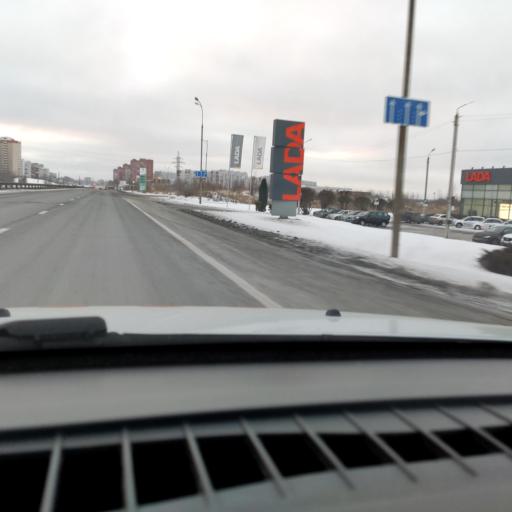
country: RU
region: Samara
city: Tol'yatti
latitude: 53.5518
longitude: 49.3371
